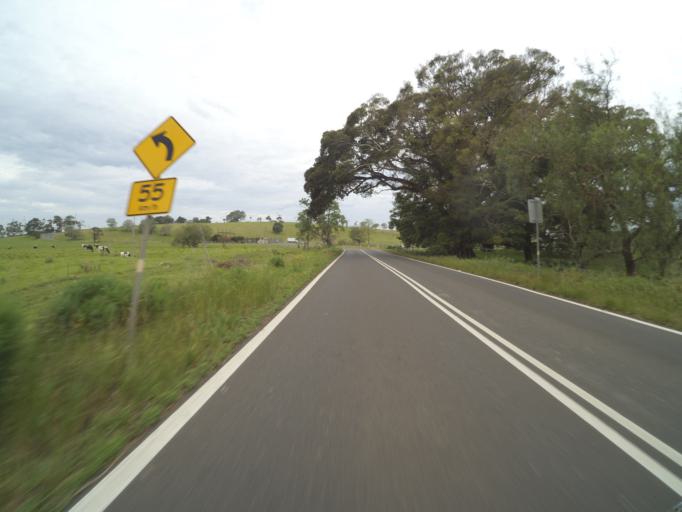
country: AU
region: New South Wales
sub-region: Kiama
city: Jamberoo
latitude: -34.6544
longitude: 150.8091
